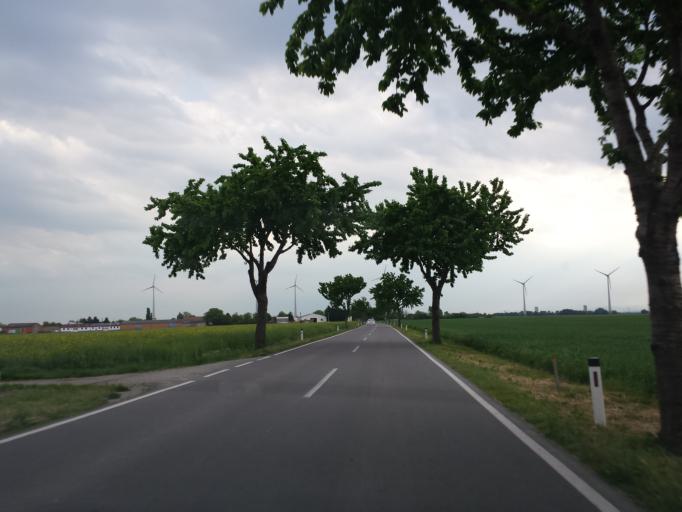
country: AT
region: Lower Austria
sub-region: Politischer Bezirk Ganserndorf
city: Grosshofen
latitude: 48.2643
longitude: 16.6224
